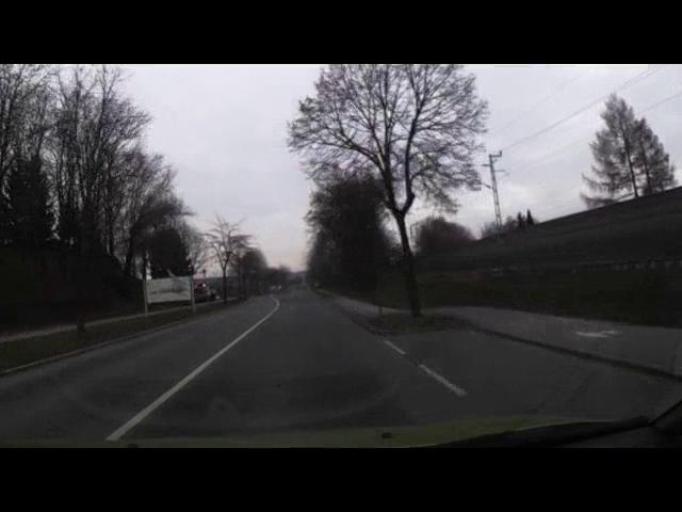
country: AT
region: Burgenland
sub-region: Eisenstadt-Umgebung
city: Neufeld an der Leitha
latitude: 47.8649
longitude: 16.3898
